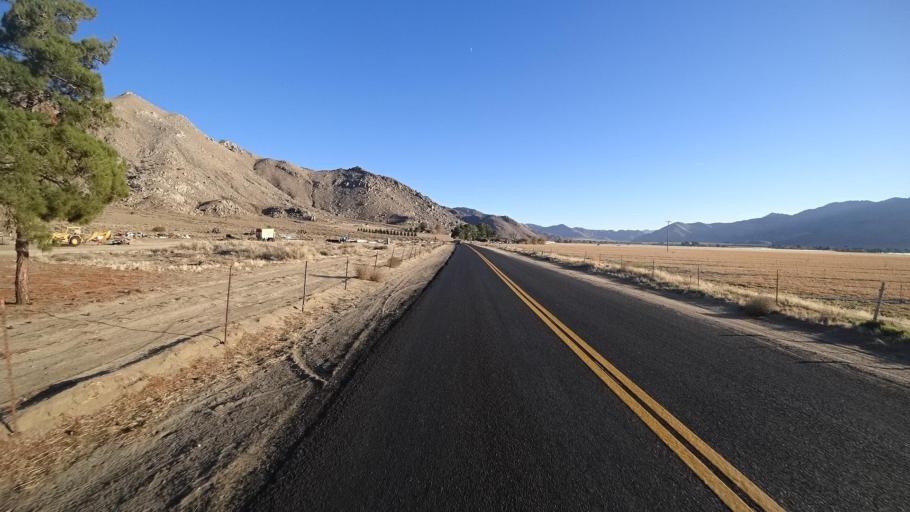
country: US
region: California
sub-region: Kern County
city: Weldon
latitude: 35.6664
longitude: -118.2605
